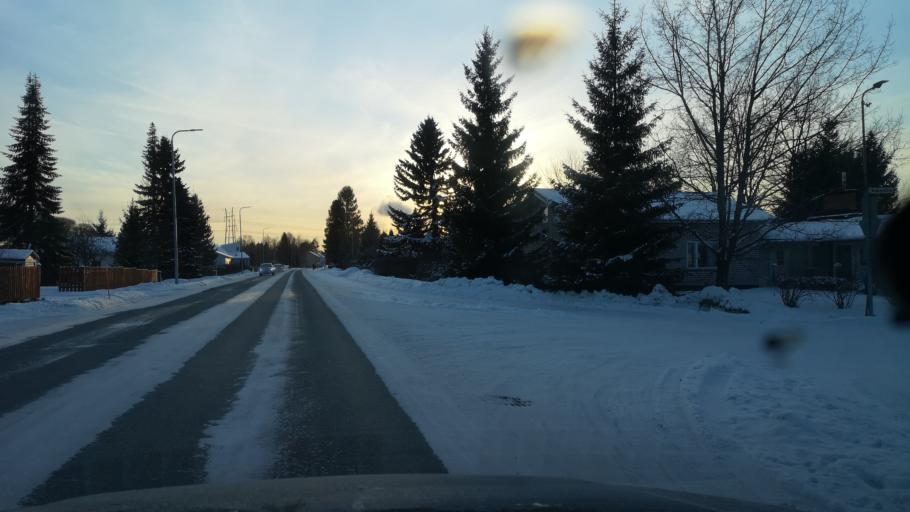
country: FI
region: Satakunta
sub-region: Pori
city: Pori
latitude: 61.5056
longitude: 21.8508
